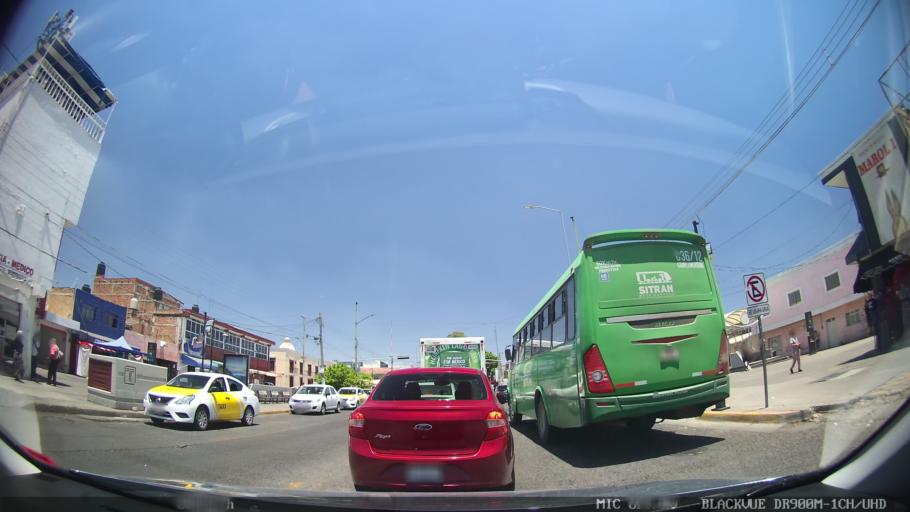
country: MX
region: Jalisco
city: Tlaquepaque
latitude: 20.6598
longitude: -103.2751
